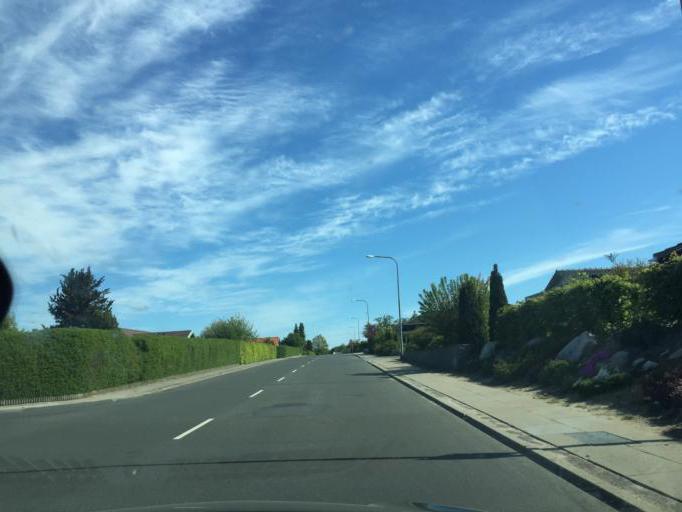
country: DK
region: South Denmark
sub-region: Kerteminde Kommune
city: Langeskov
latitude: 55.3540
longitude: 10.5925
